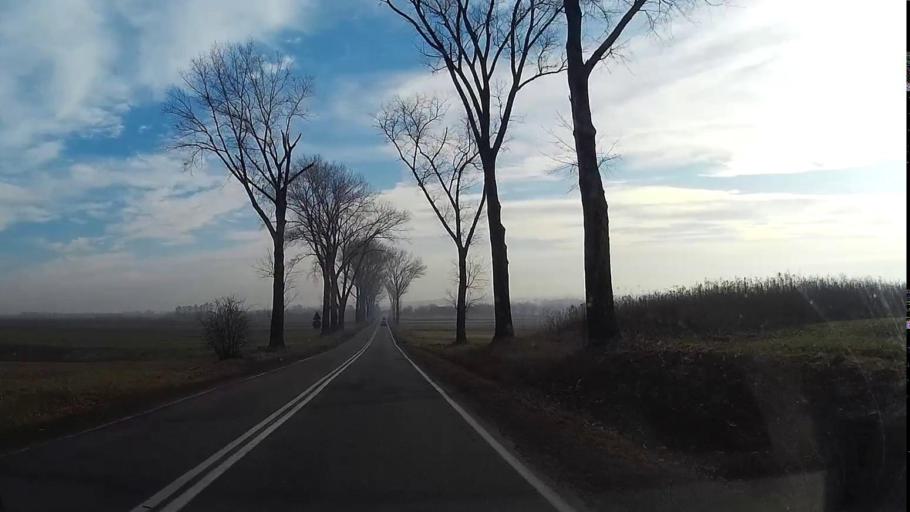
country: PL
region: Lesser Poland Voivodeship
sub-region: Powiat krakowski
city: Kaszow
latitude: 50.0395
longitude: 19.7023
